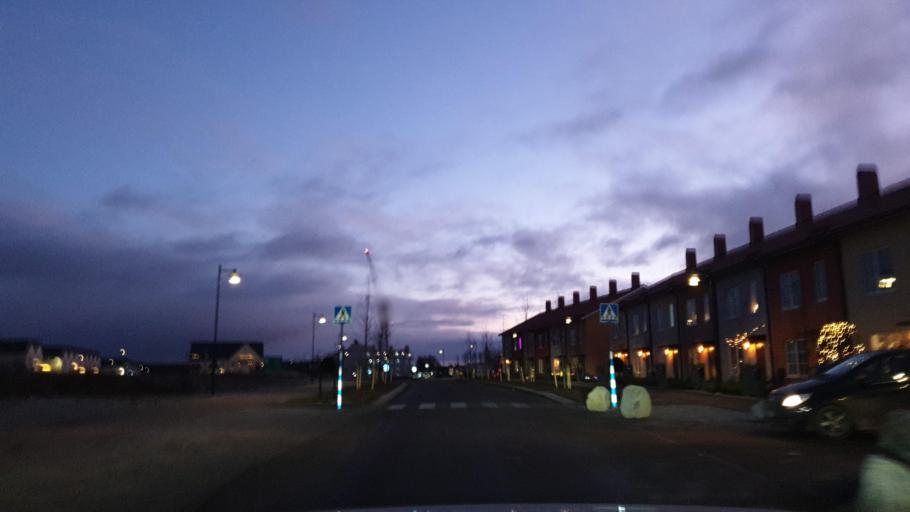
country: SE
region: Stockholm
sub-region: Sigtuna Kommun
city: Marsta
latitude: 59.6095
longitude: 17.7951
